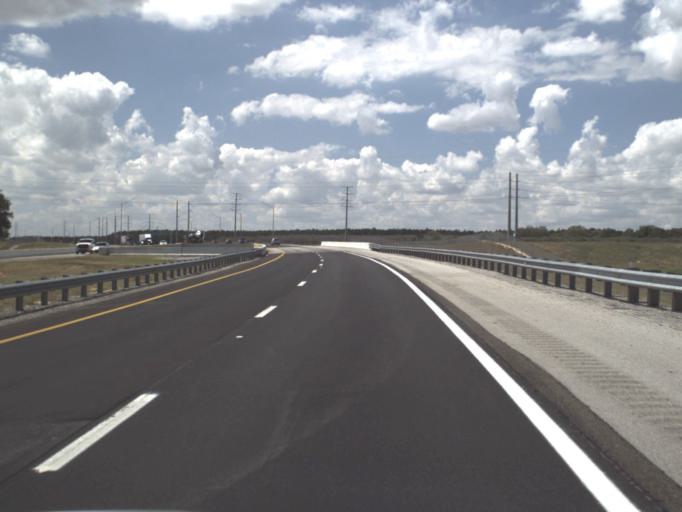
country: US
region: Florida
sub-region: Orange County
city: Oakland
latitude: 28.4841
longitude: -81.6295
